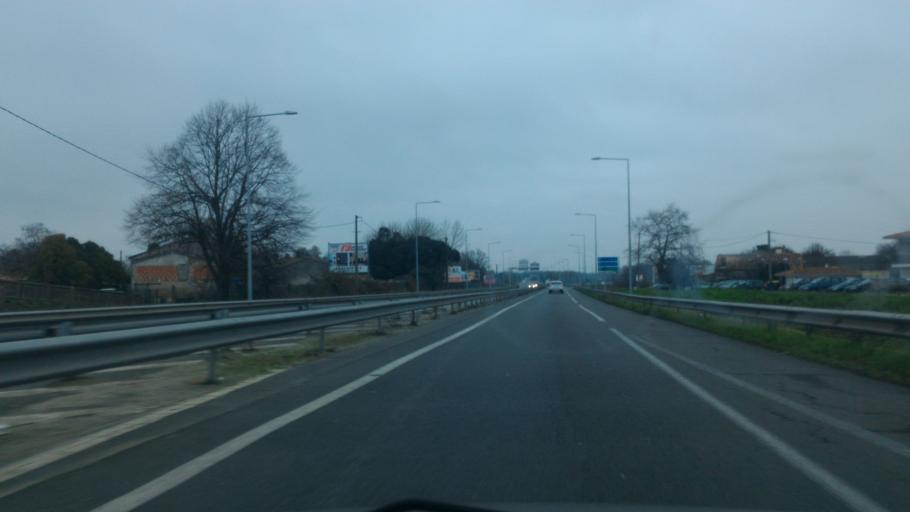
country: FR
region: Aquitaine
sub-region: Departement de la Gironde
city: Saint-Gervais
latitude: 45.0035
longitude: -0.4349
